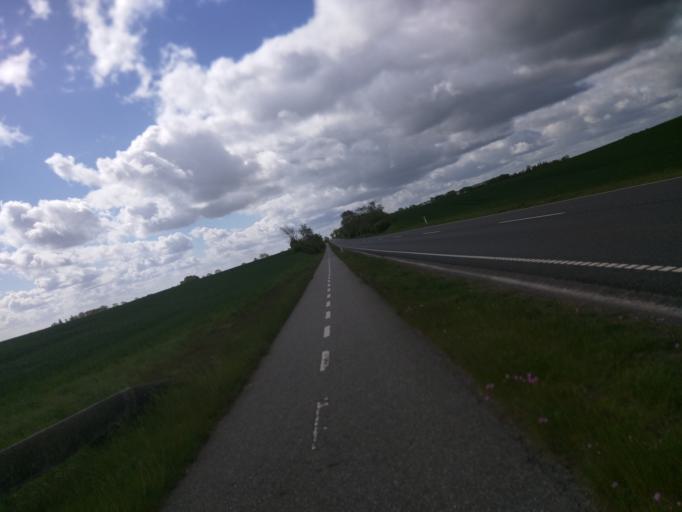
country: DK
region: Central Jutland
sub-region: Silkeborg Kommune
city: Kjellerup
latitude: 56.3154
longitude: 9.4213
